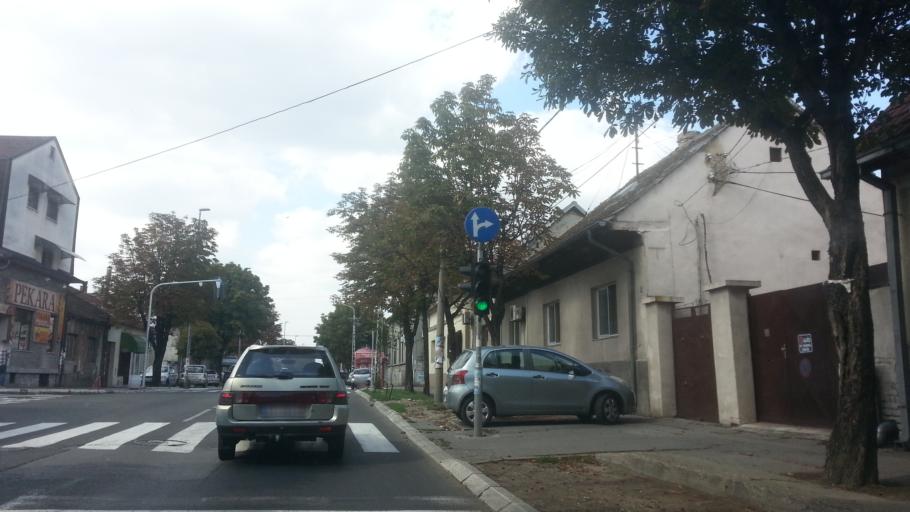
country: RS
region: Central Serbia
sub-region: Belgrade
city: Zemun
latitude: 44.8488
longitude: 20.4039
